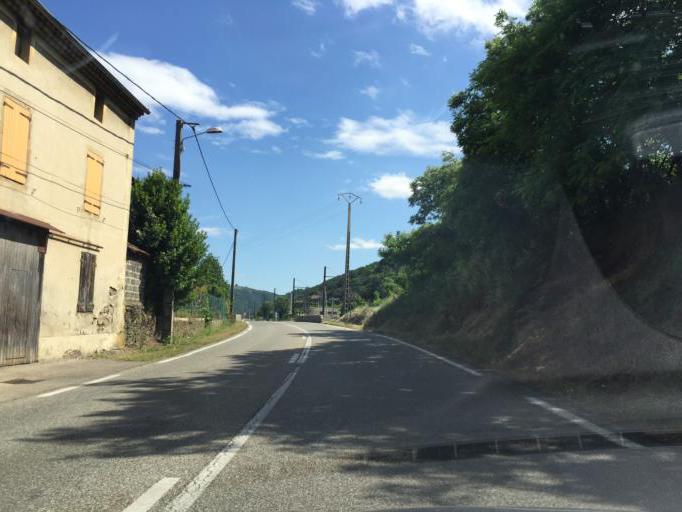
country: FR
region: Rhone-Alpes
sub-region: Departement de la Drome
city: Saint-Vallier
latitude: 45.1697
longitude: 4.8054
